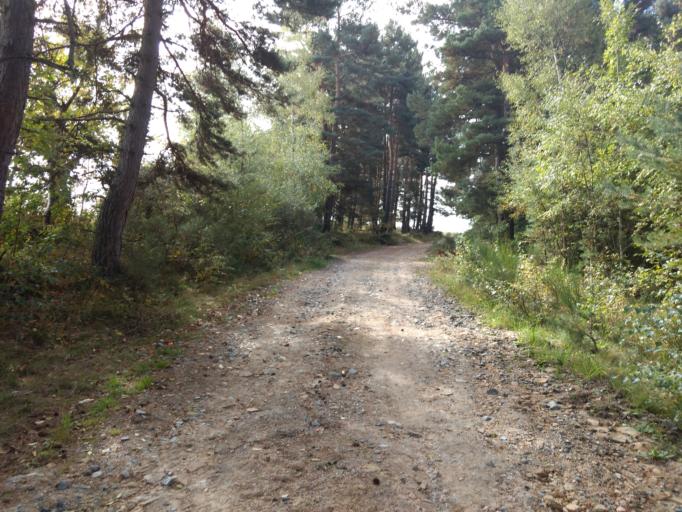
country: FR
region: Auvergne
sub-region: Departement du Cantal
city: Chaudes-Aigues
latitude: 44.8546
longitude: 2.9938
